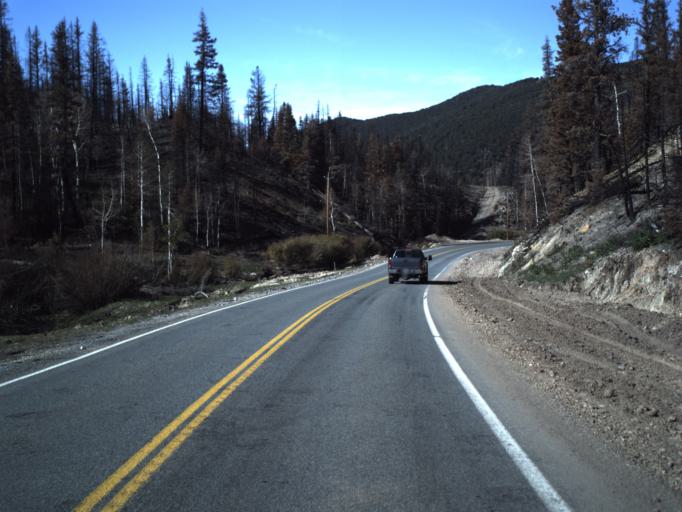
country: US
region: Utah
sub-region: Iron County
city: Parowan
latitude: 37.7447
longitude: -112.8382
